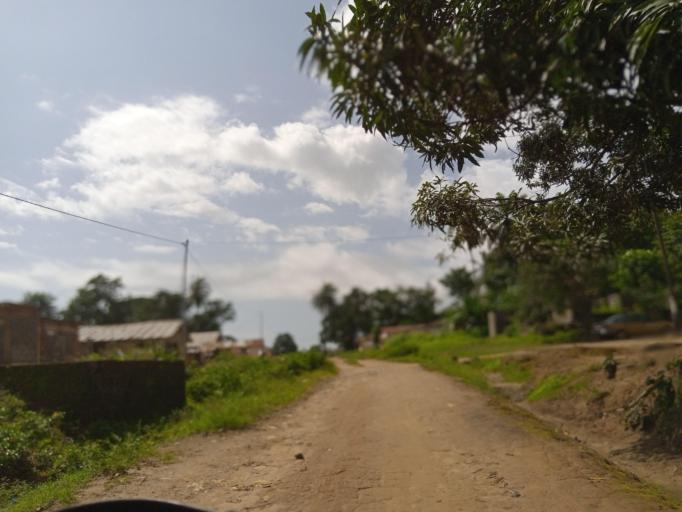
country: SL
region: Northern Province
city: Masoyila
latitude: 8.6078
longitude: -13.2052
